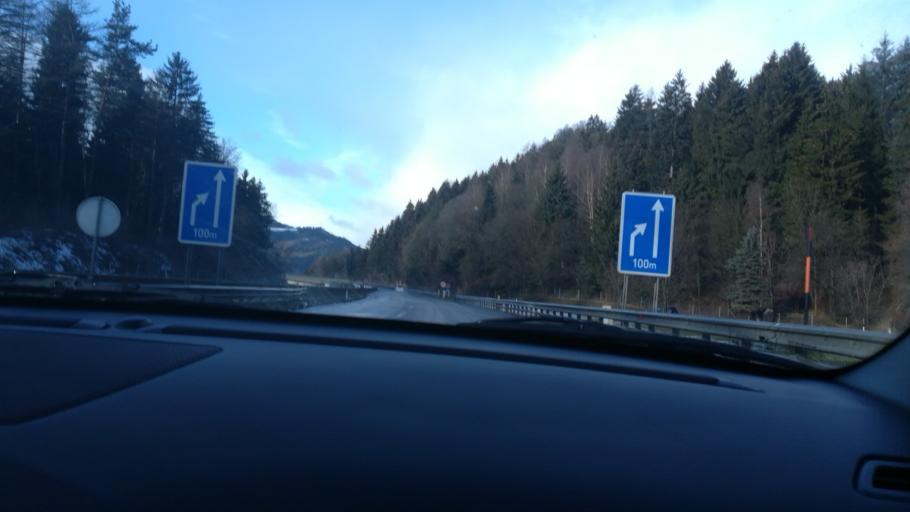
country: AT
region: Styria
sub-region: Politischer Bezirk Murtal
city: Judenburg
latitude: 47.1765
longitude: 14.6469
